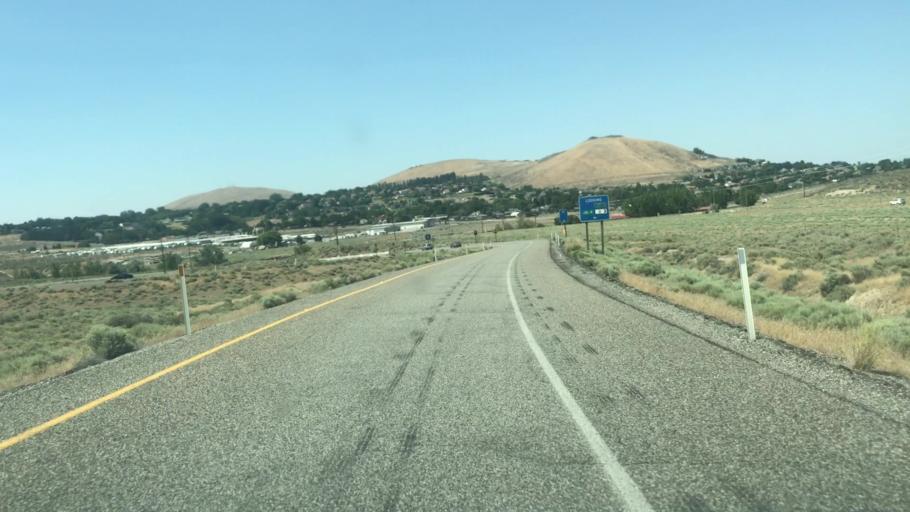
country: US
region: Washington
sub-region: Benton County
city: Richland
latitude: 46.1926
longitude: -119.2632
